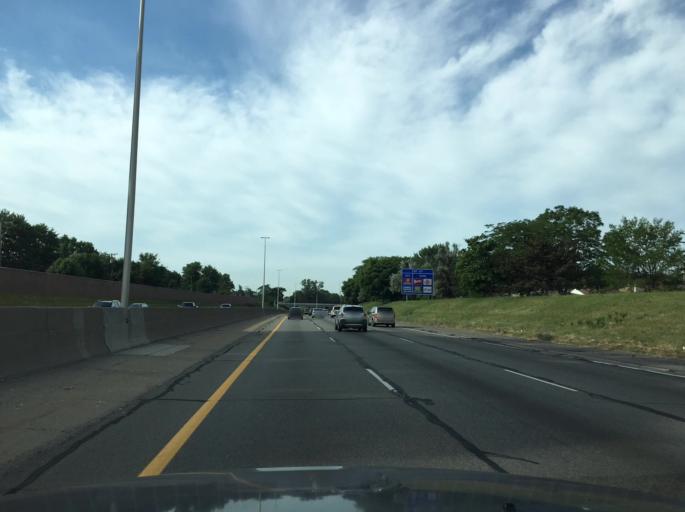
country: US
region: Michigan
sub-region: Macomb County
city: Roseville
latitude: 42.4765
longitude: -82.9166
